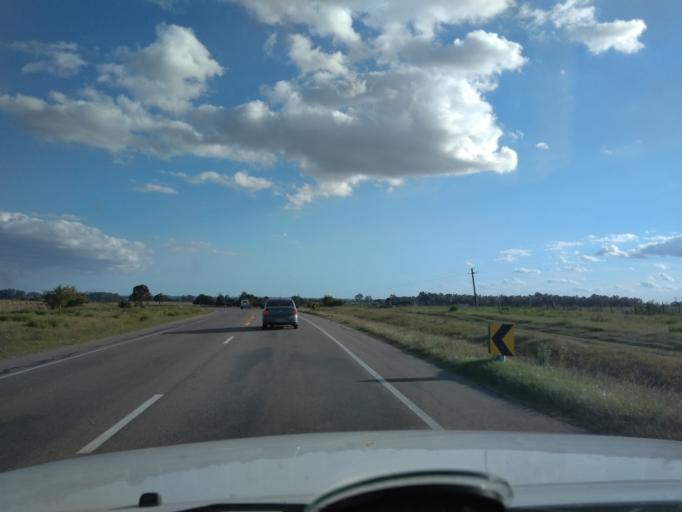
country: UY
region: Florida
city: Cardal
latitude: -34.3161
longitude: -56.2412
